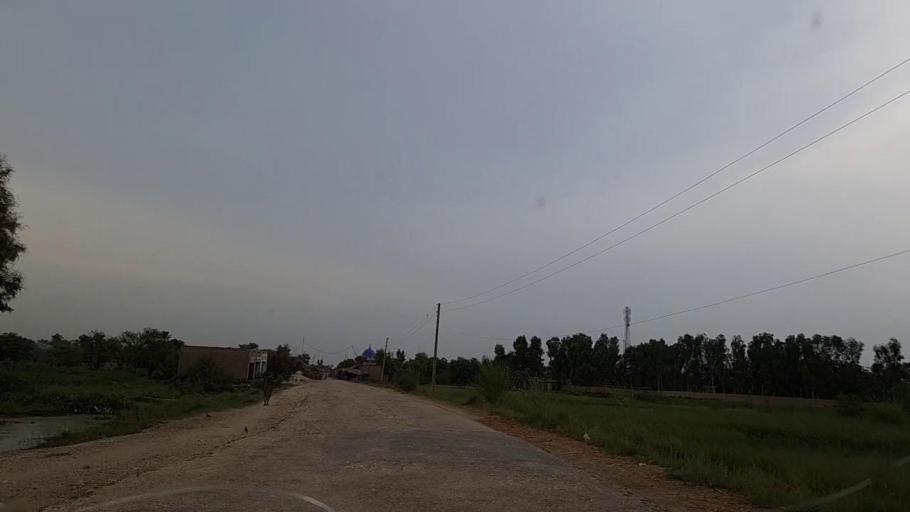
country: PK
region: Sindh
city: Mirpur Mathelo
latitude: 27.8958
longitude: 69.6554
